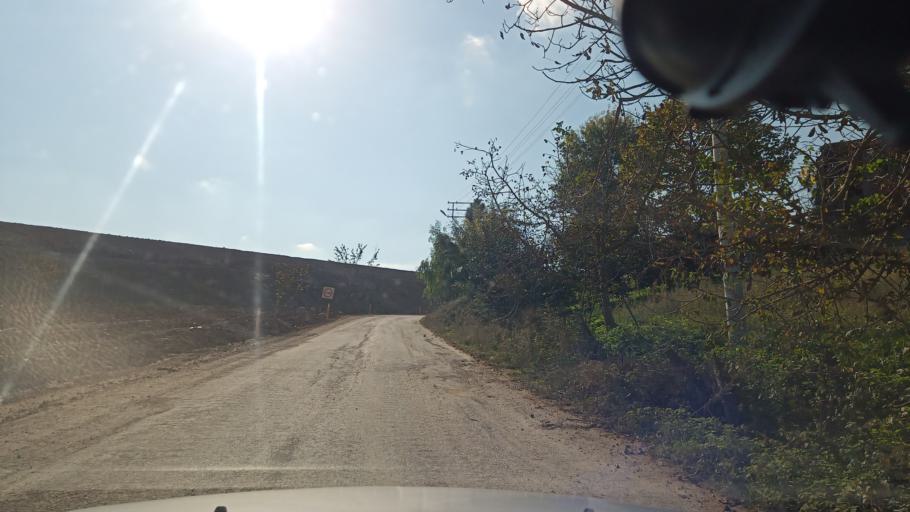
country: TR
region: Sakarya
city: Ferizli
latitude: 41.1035
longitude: 30.4762
